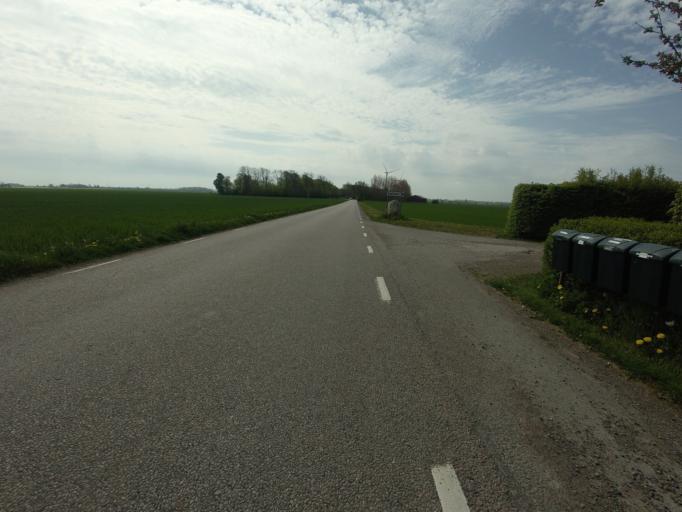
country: SE
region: Skane
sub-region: Hoganas Kommun
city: Hoganas
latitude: 56.2453
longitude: 12.5734
